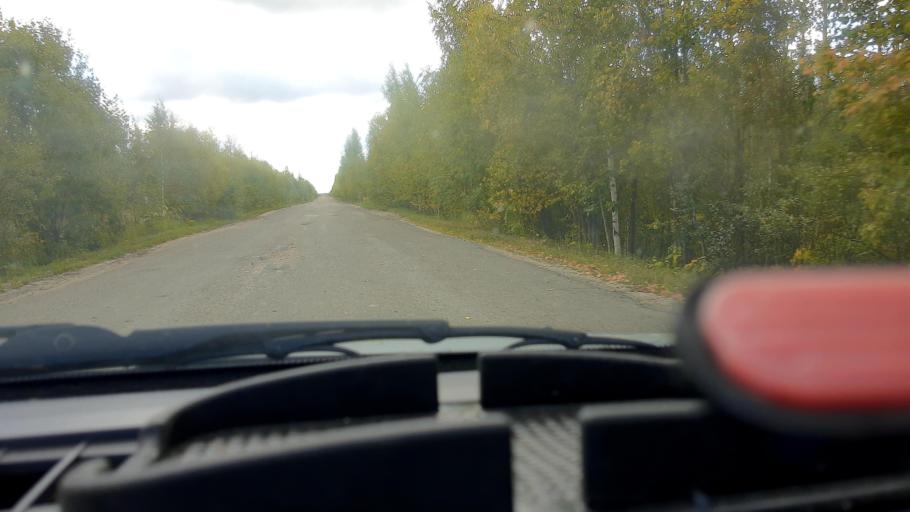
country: RU
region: Mariy-El
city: Kilemary
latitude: 56.9018
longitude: 46.7413
